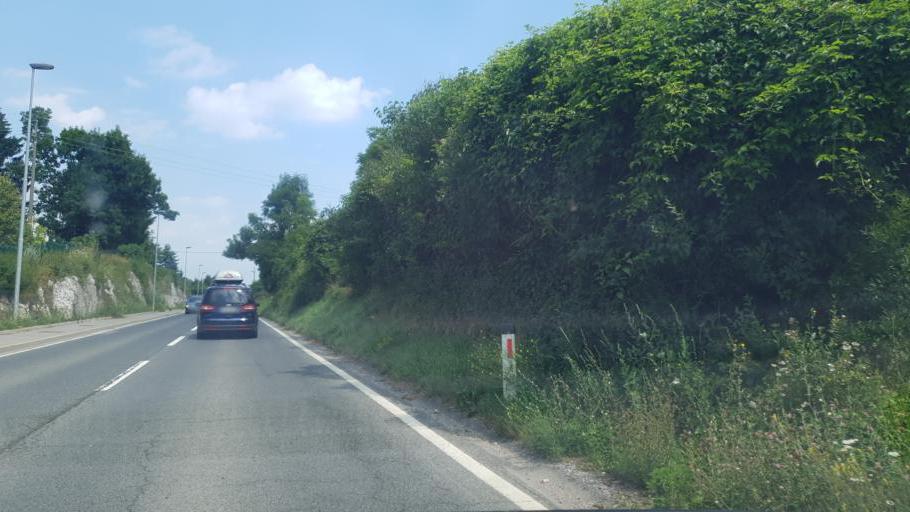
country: SI
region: Pivka
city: Pivka
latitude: 45.7317
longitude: 14.1862
